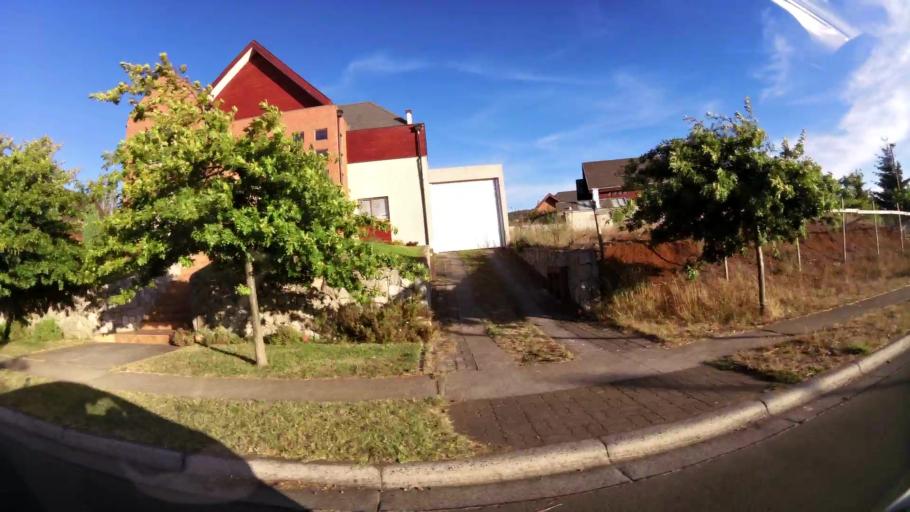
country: CL
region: Biobio
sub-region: Provincia de Concepcion
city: Concepcion
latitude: -36.8621
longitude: -73.1001
